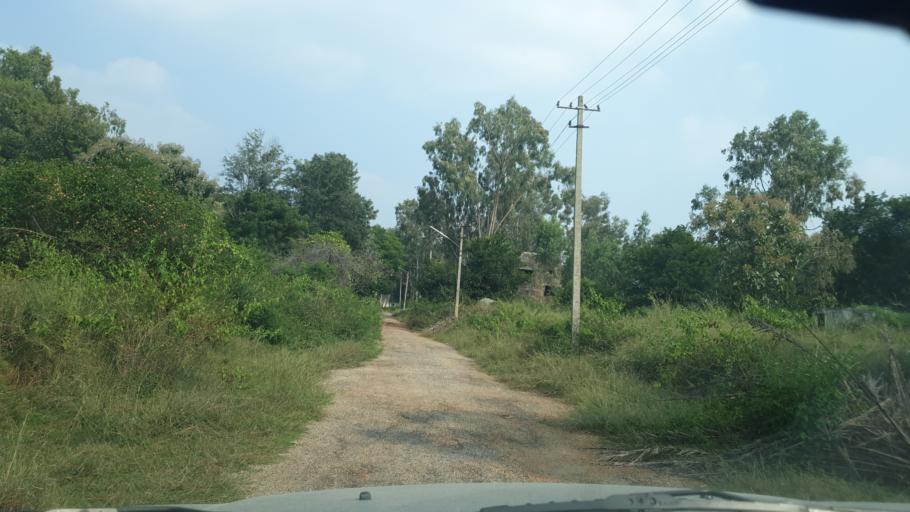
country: IN
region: Karnataka
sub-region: Bangalore Urban
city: Yelahanka
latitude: 13.0706
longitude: 77.6673
